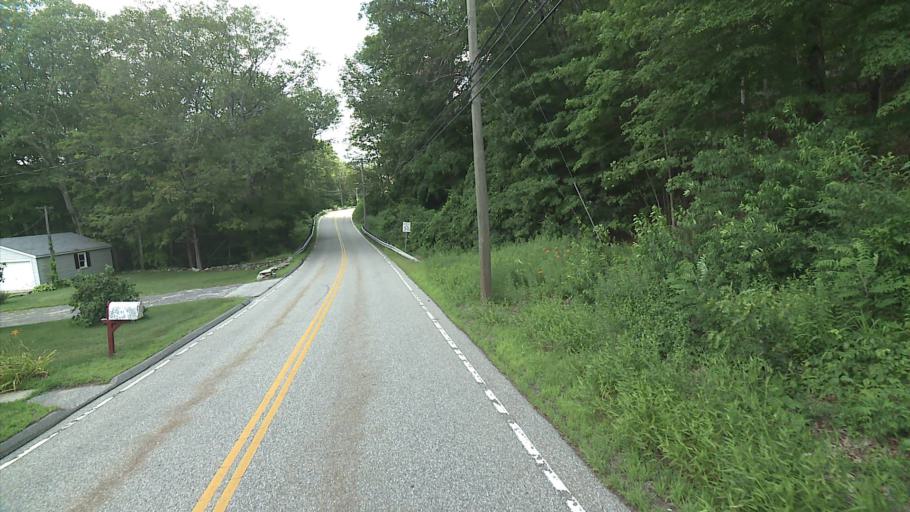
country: US
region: Connecticut
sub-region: New London County
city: Baltic
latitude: 41.6151
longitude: -72.0730
